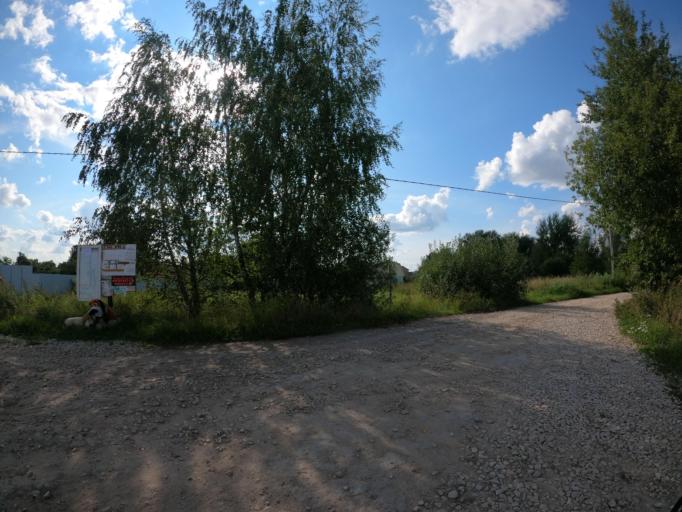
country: RU
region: Moskovskaya
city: Troitskoye
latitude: 55.2390
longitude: 38.4889
